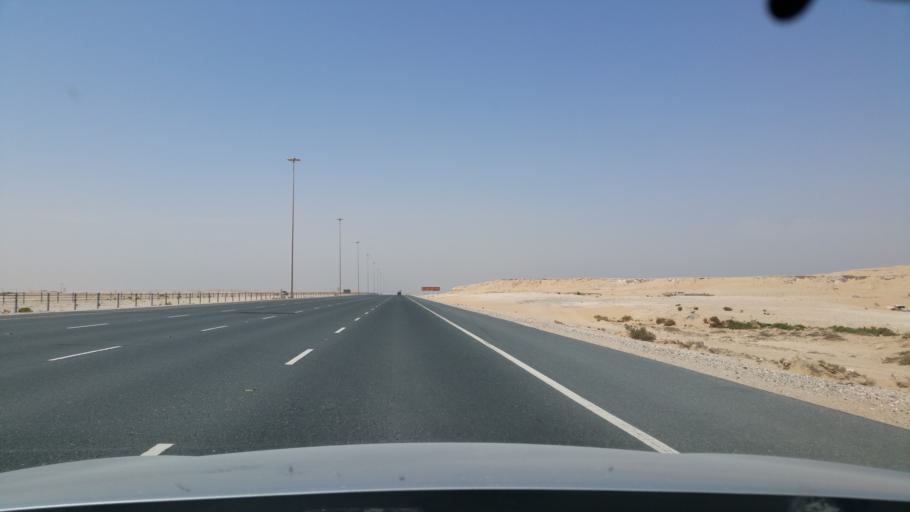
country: QA
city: Umm Bab
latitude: 24.8728
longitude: 50.9163
